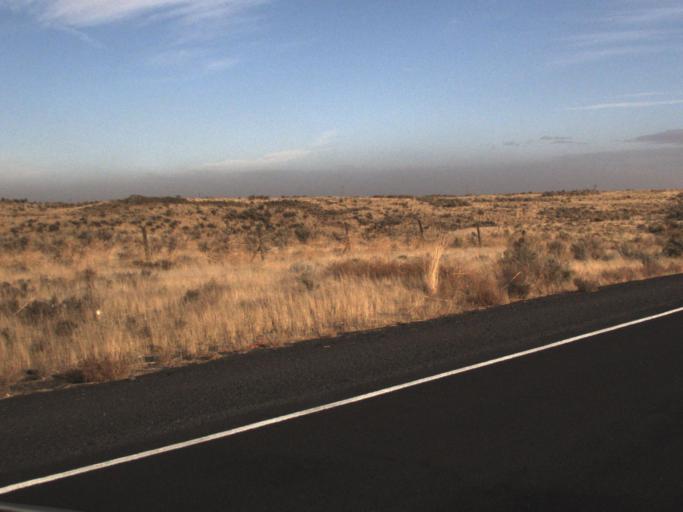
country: US
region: Washington
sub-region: Grant County
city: Warden
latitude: 47.3203
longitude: -118.8598
